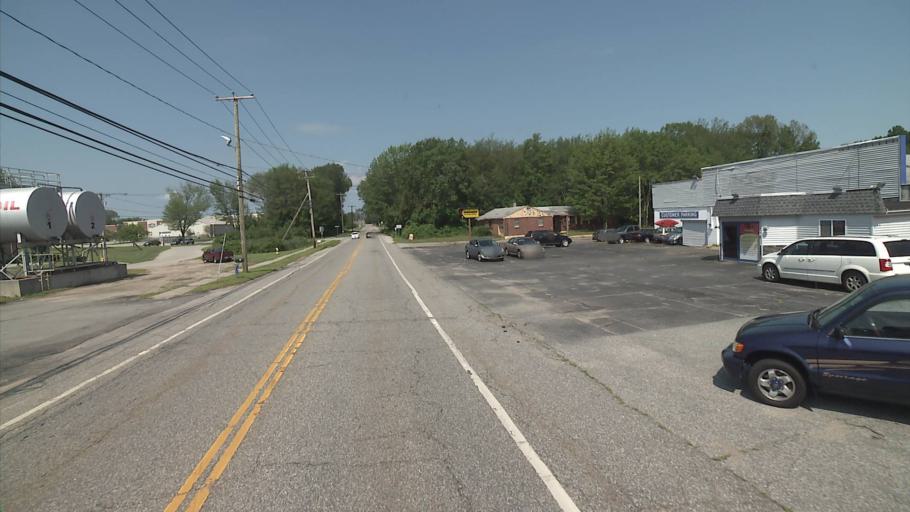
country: US
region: Connecticut
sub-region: New London County
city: Colchester
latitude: 41.5748
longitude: -72.3148
